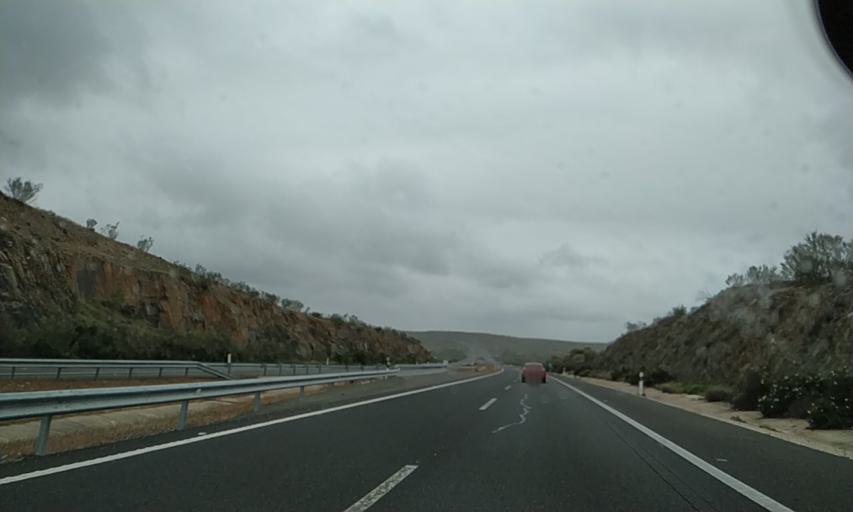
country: ES
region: Extremadura
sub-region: Provincia de Caceres
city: Hinojal
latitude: 39.7279
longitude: -6.4121
